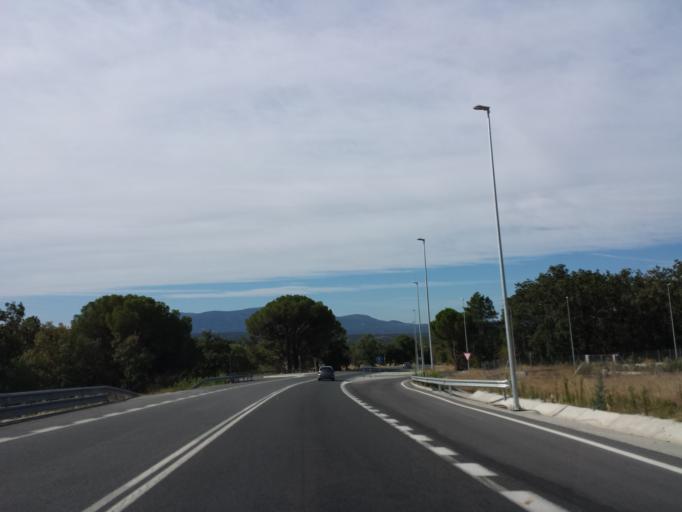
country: ES
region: Castille and Leon
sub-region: Provincia de Avila
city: Piedralaves
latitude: 40.2951
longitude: -4.7214
